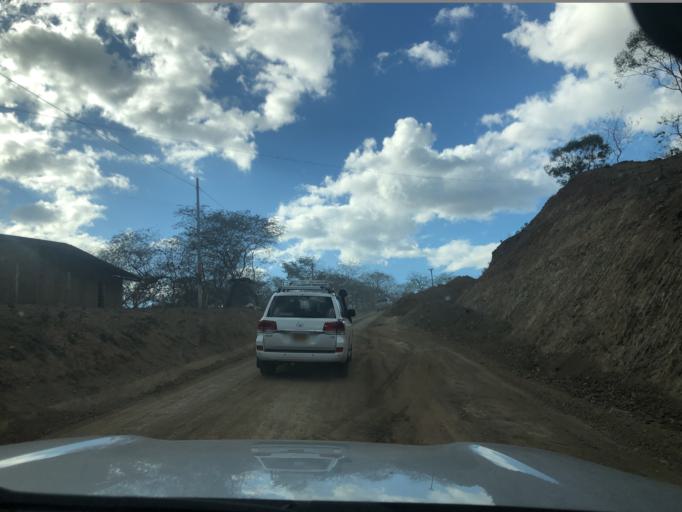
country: NI
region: Nueva Segovia
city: Ocotal
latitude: 13.6543
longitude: -86.6141
